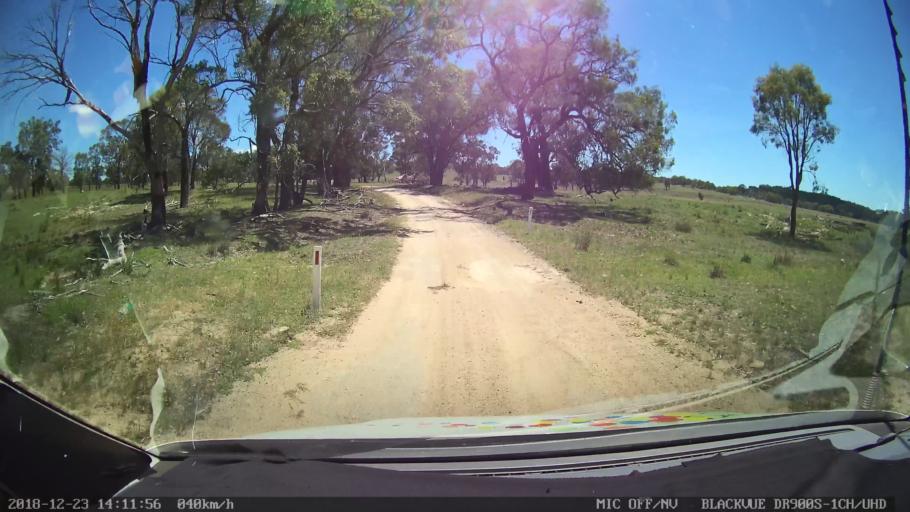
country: AU
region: New South Wales
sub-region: Tamworth Municipality
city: Manilla
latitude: -30.6531
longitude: 151.0475
